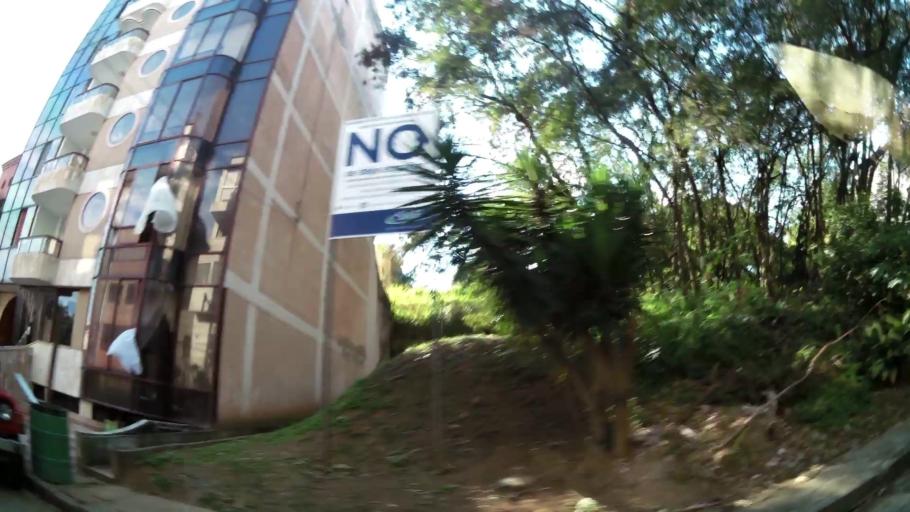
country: CO
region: Valle del Cauca
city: Cali
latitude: 3.4458
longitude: -76.5498
